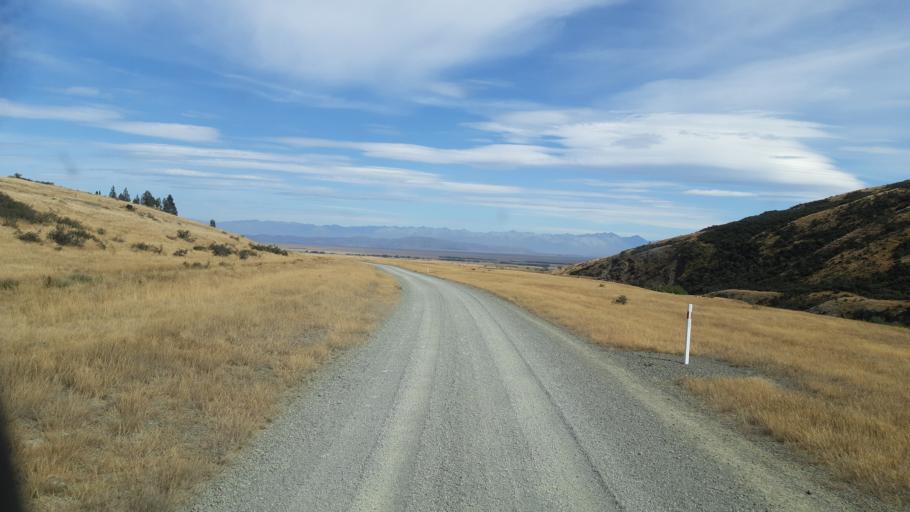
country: NZ
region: Canterbury
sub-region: Timaru District
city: Pleasant Point
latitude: -44.1938
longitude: 170.5724
